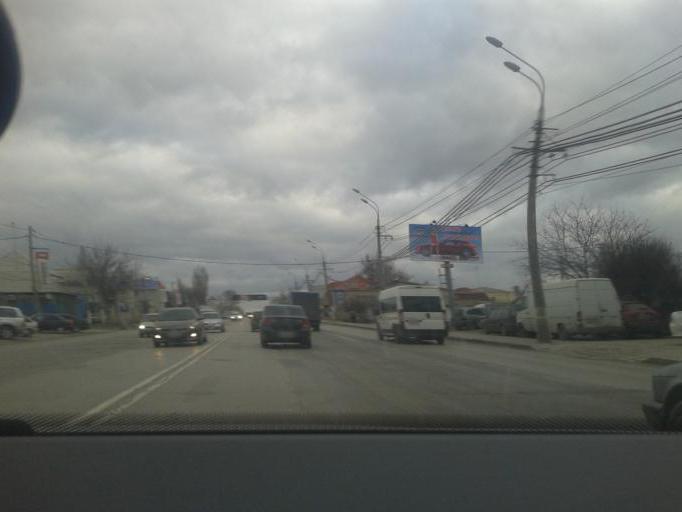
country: RU
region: Volgograd
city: Volgograd
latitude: 48.6935
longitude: 44.4643
